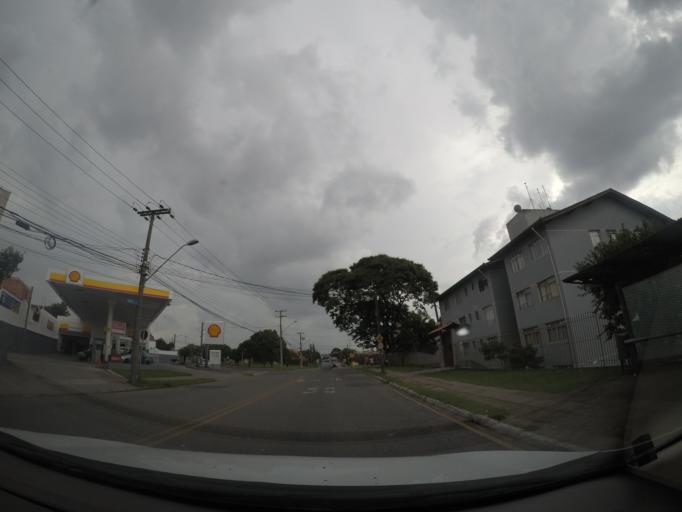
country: BR
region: Parana
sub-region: Sao Jose Dos Pinhais
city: Sao Jose dos Pinhais
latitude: -25.5309
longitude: -49.2447
